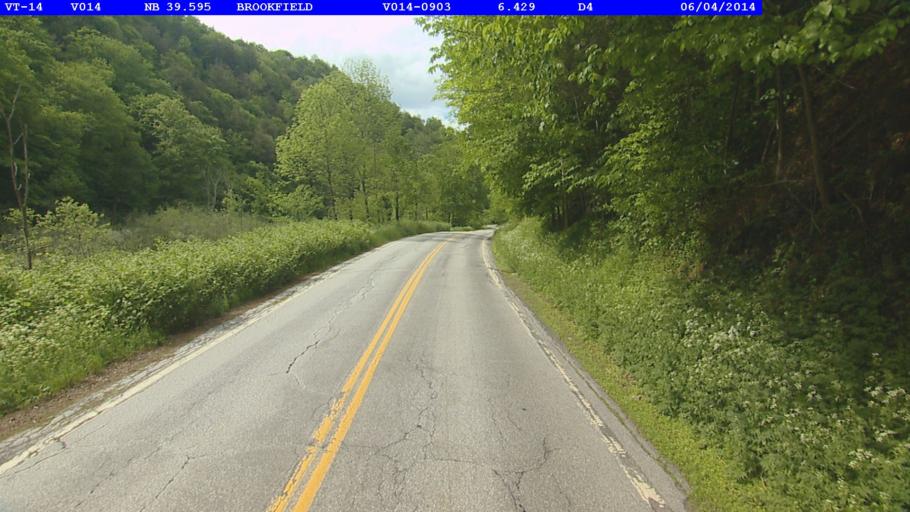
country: US
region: Vermont
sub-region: Orange County
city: Williamstown
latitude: 44.0678
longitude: -72.5678
